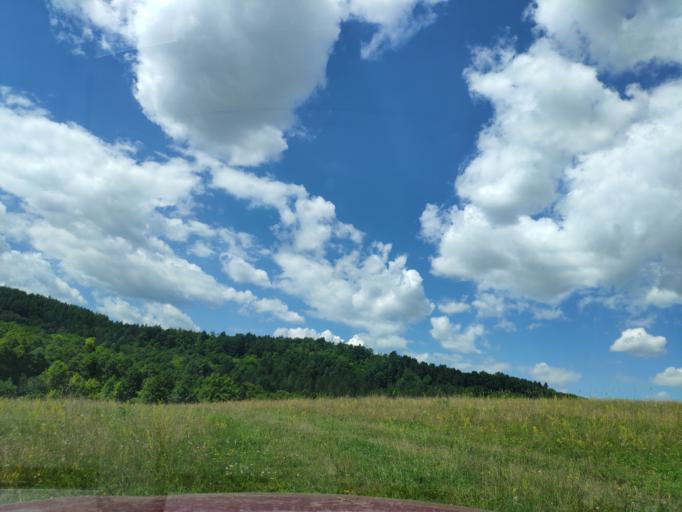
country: HU
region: Borsod-Abauj-Zemplen
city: Arlo
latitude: 48.2614
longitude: 20.1723
